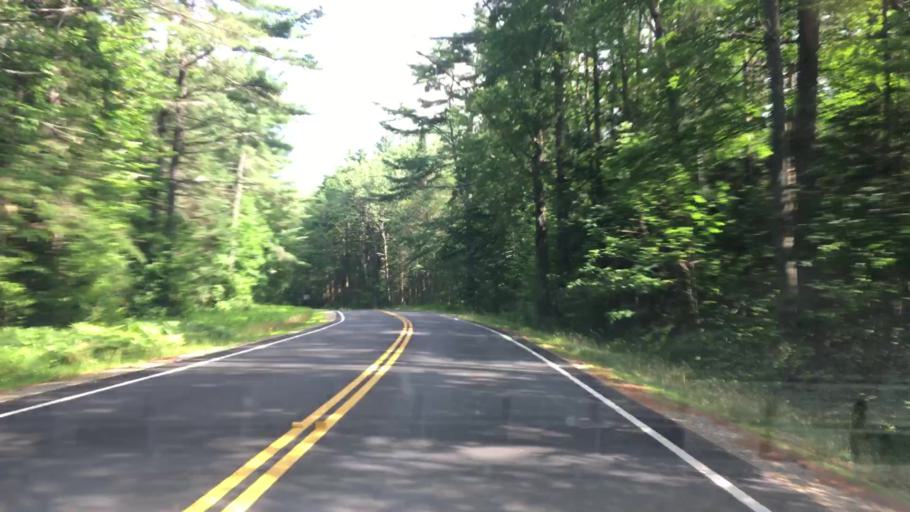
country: US
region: New Hampshire
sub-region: Grafton County
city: North Haverhill
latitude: 44.1024
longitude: -71.8646
